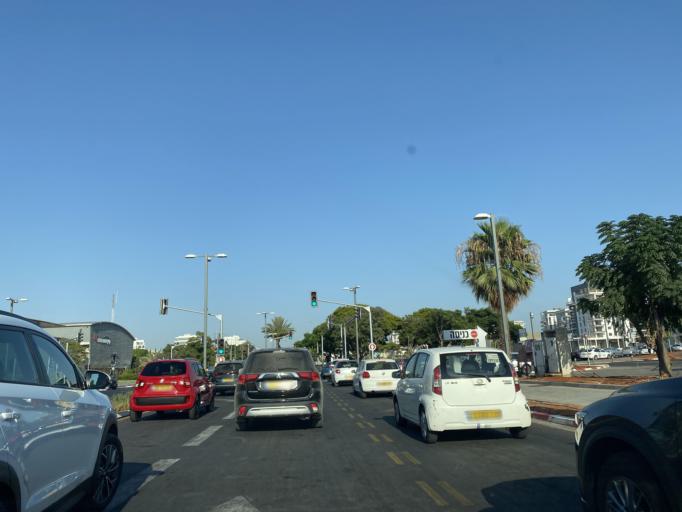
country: IL
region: Tel Aviv
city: Herzliyya
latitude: 32.1641
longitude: 34.8223
